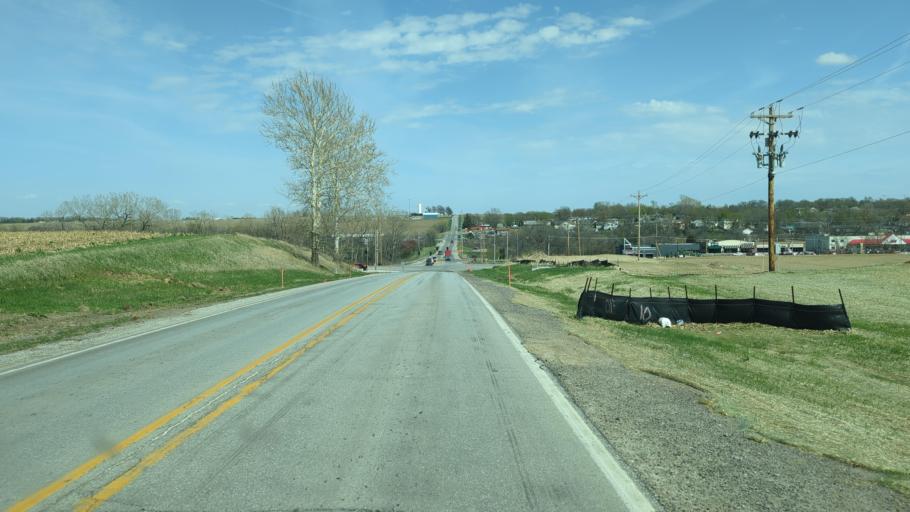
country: US
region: Nebraska
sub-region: Sarpy County
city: Springfield
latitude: 41.0891
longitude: -96.1415
